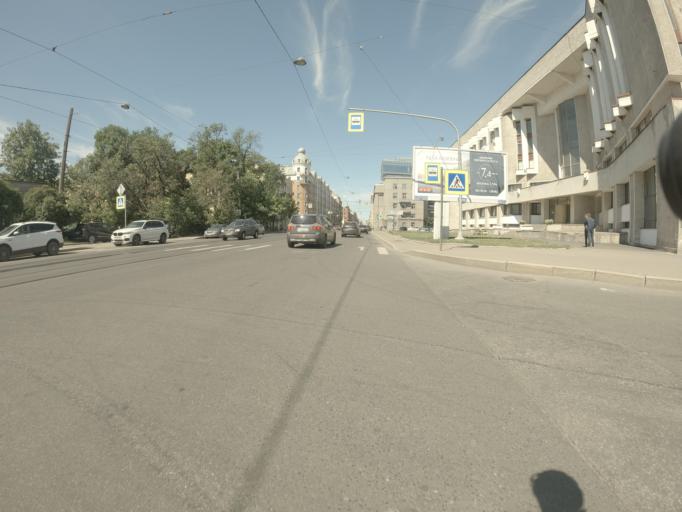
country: RU
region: St.-Petersburg
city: Centralniy
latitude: 59.9277
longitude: 30.3832
